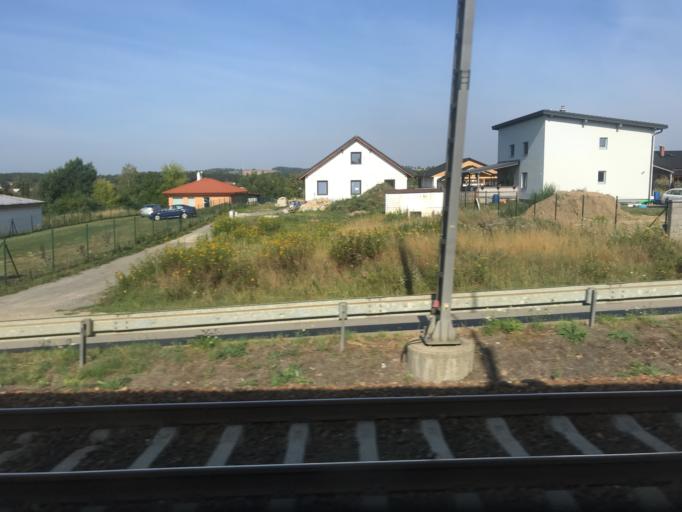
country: CZ
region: Jihocesky
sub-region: Okres Tabor
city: Sezimovo Usti
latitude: 49.3828
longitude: 14.6985
